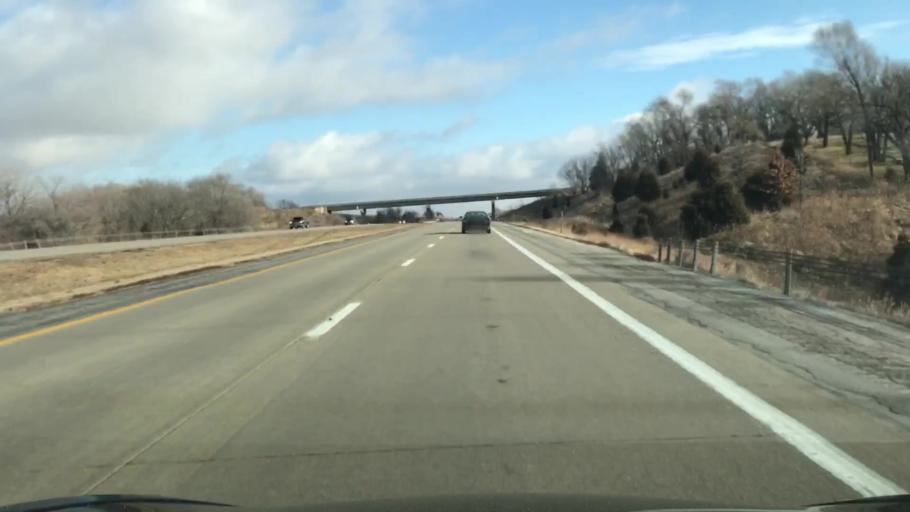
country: US
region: Iowa
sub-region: Cass County
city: Atlantic
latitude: 41.4970
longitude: -94.8379
